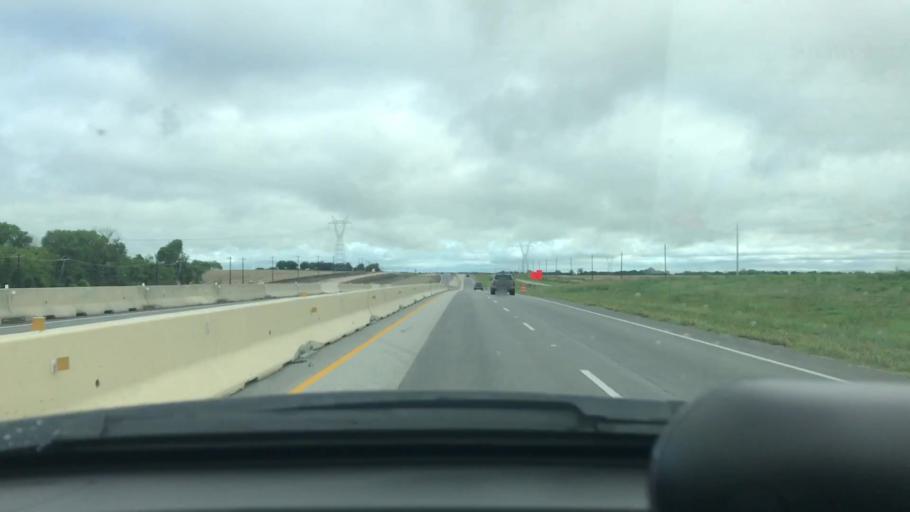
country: US
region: Texas
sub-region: Collin County
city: Anna
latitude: 33.3637
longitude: -96.5831
